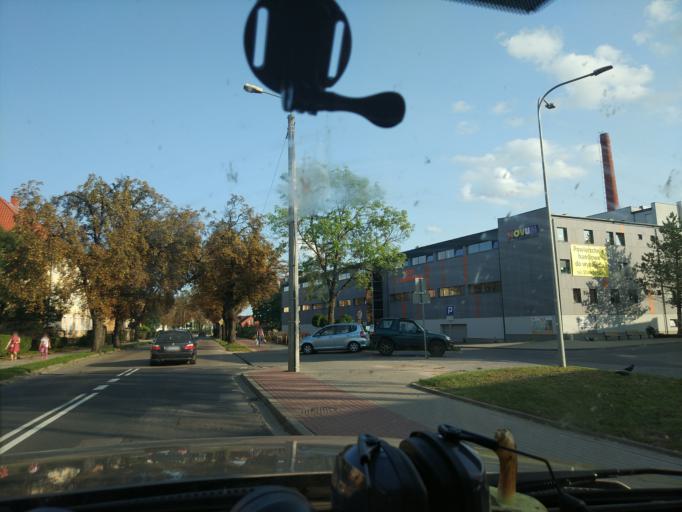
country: PL
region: Warmian-Masurian Voivodeship
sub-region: Powiat szczycienski
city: Szczytno
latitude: 53.5630
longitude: 20.9887
